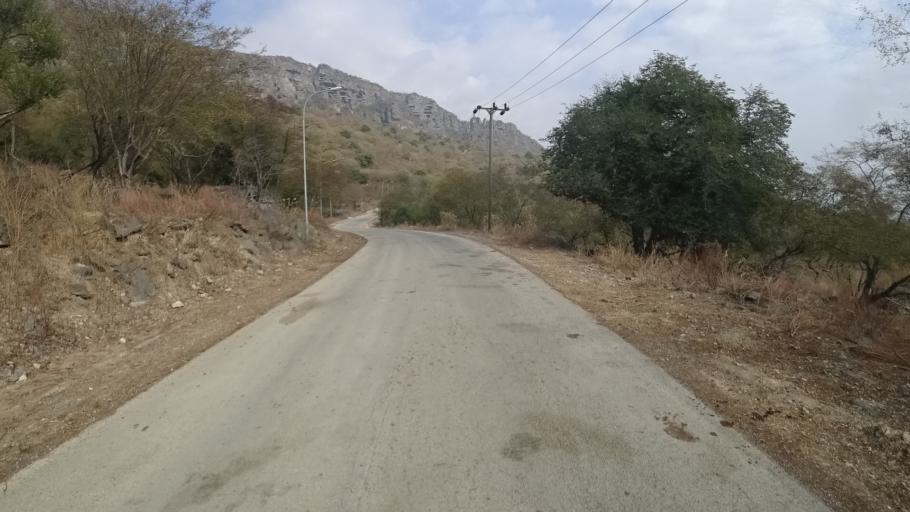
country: YE
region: Al Mahrah
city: Hawf
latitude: 16.7178
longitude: 53.2551
